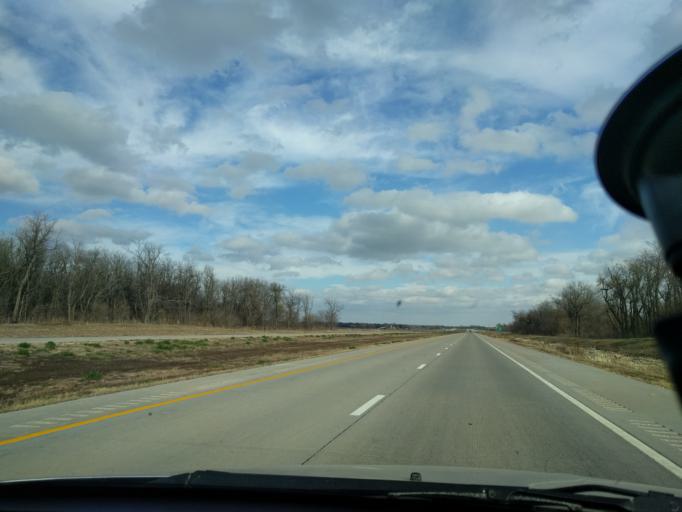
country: US
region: Kansas
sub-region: Reno County
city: Buhler
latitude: 38.1481
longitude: -97.8624
